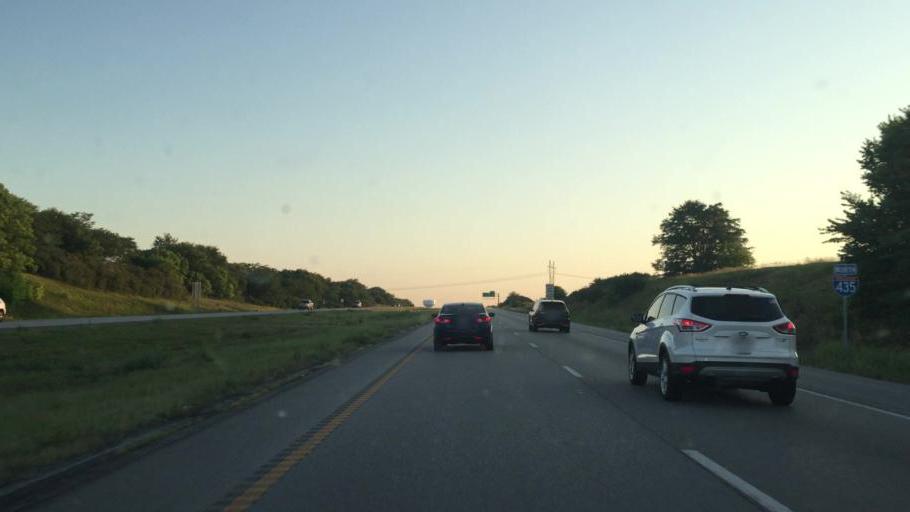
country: US
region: Missouri
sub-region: Clay County
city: Pleasant Valley
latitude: 39.2906
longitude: -94.5101
